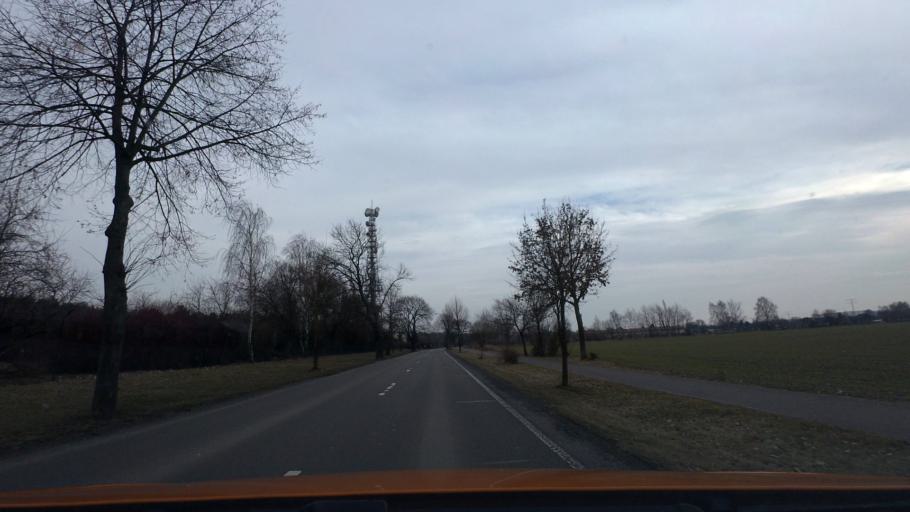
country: DE
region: Berlin
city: Falkenberg
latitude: 52.5882
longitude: 13.5586
